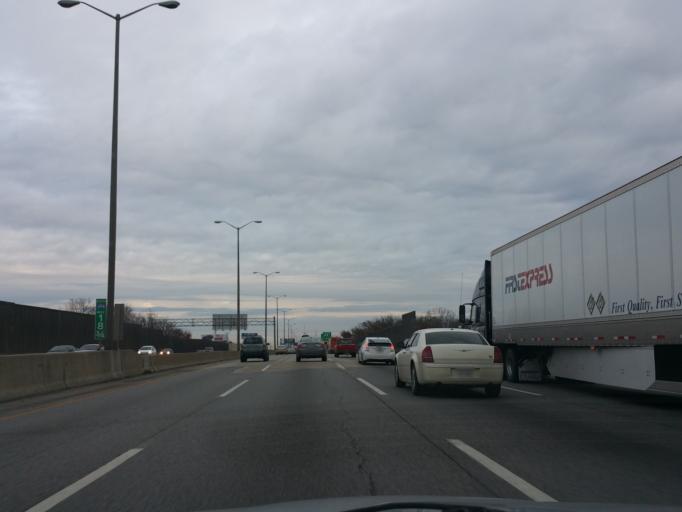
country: US
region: Illinois
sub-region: Cook County
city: Hickory Hills
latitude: 41.7338
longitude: -87.8193
